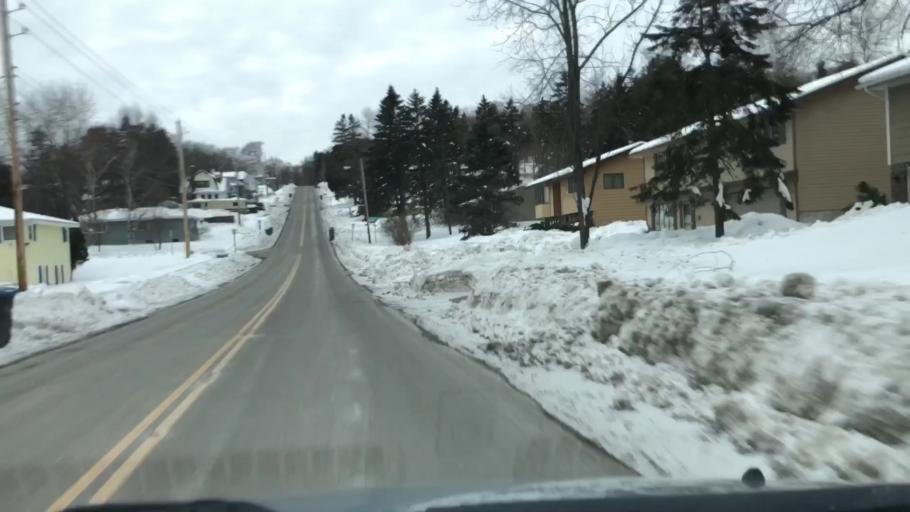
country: US
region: Minnesota
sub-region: Saint Louis County
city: Arnold
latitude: 46.8367
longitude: -92.0588
